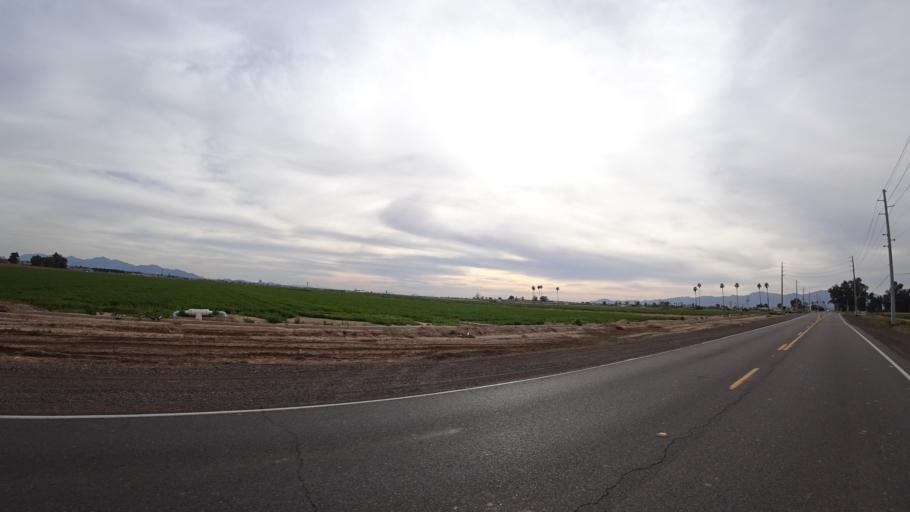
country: US
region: Arizona
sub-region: Maricopa County
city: El Mirage
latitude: 33.5657
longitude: -112.3555
